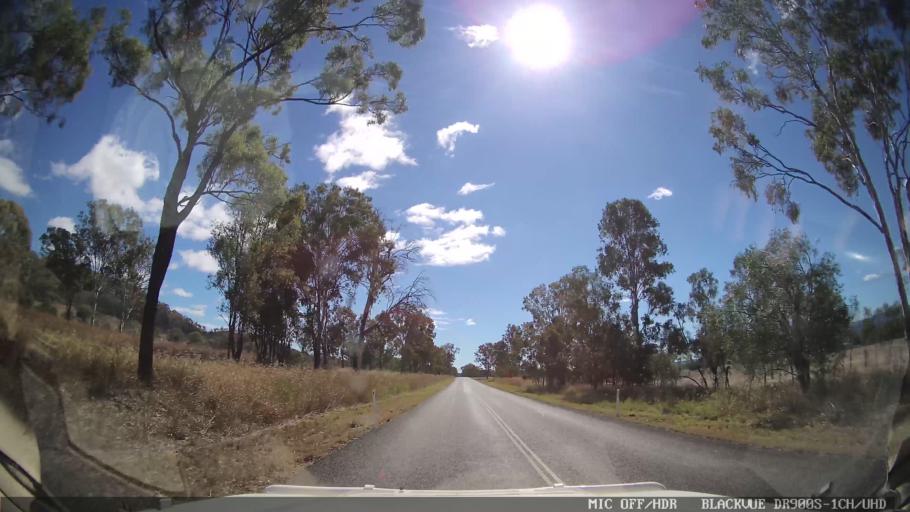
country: AU
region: Queensland
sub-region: Gladstone
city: Toolooa
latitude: -24.4524
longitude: 151.3461
